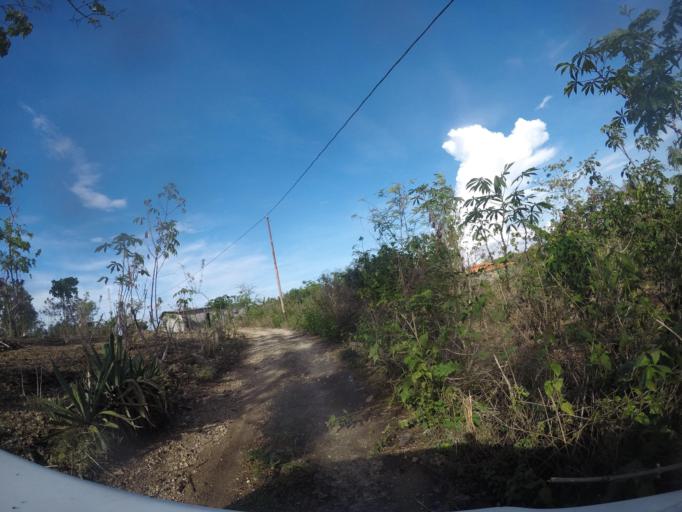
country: TL
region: Baucau
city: Baucau
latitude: -8.4898
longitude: 126.4532
